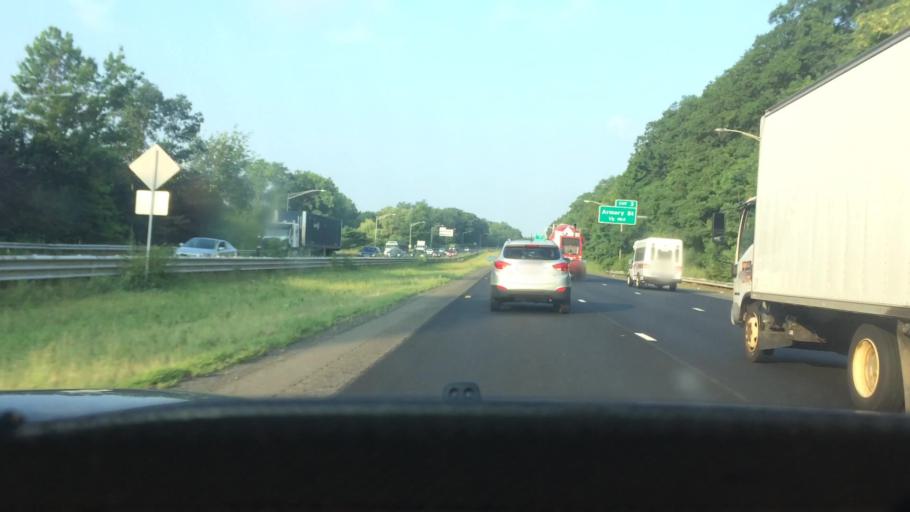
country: US
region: Massachusetts
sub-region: Hampden County
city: Springfield
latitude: 42.1249
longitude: -72.5705
